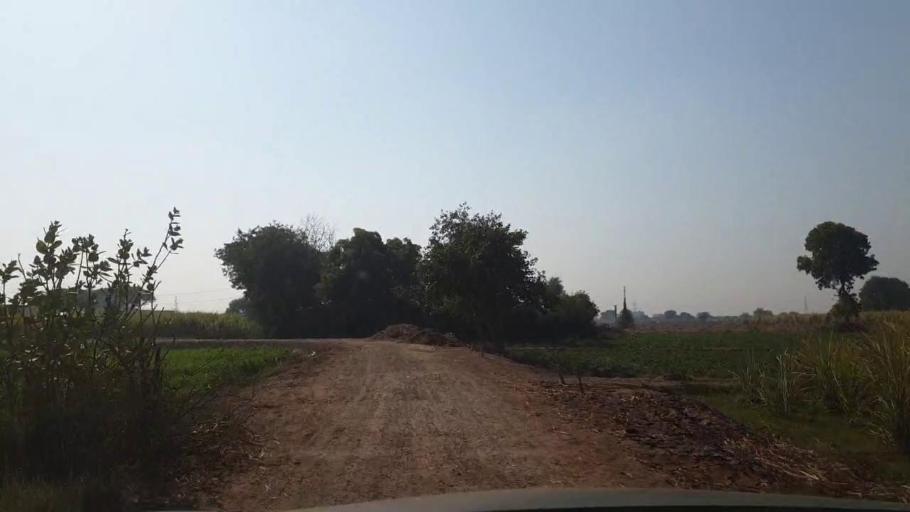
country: PK
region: Sindh
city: Tando Allahyar
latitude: 25.5142
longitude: 68.6982
